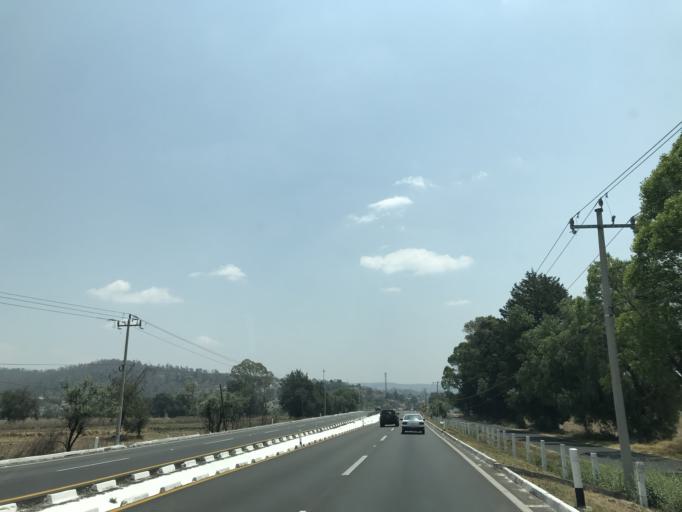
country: MX
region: Tlaxcala
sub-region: Ixtacuixtla de Mariano Matamoros
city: Santa Justina Ecatepec
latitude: 19.3285
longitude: -98.3588
